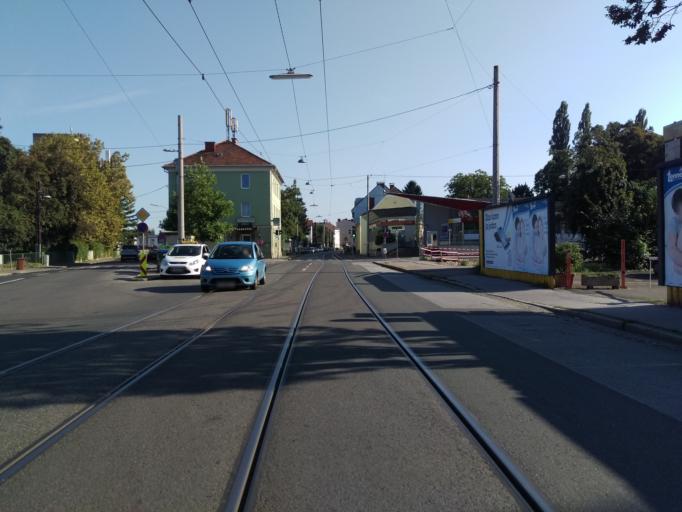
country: AT
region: Styria
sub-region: Graz Stadt
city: Graz
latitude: 47.0529
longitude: 15.4324
